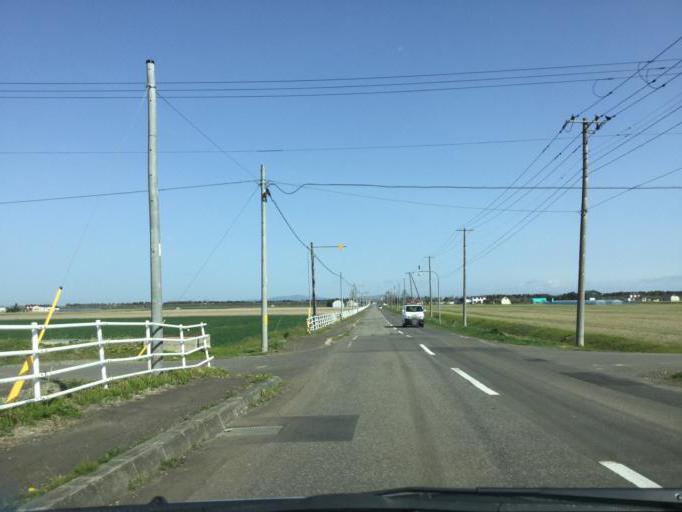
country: JP
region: Hokkaido
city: Iwamizawa
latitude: 43.1466
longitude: 141.7201
